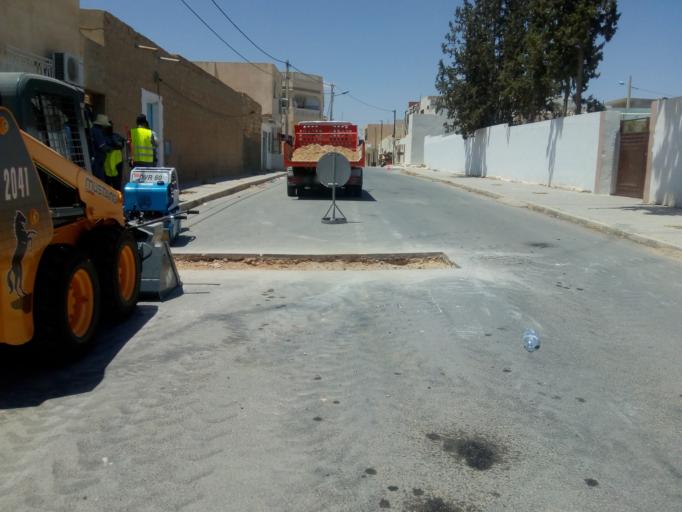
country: TN
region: Qabis
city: Matmata
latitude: 33.6201
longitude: 10.2812
